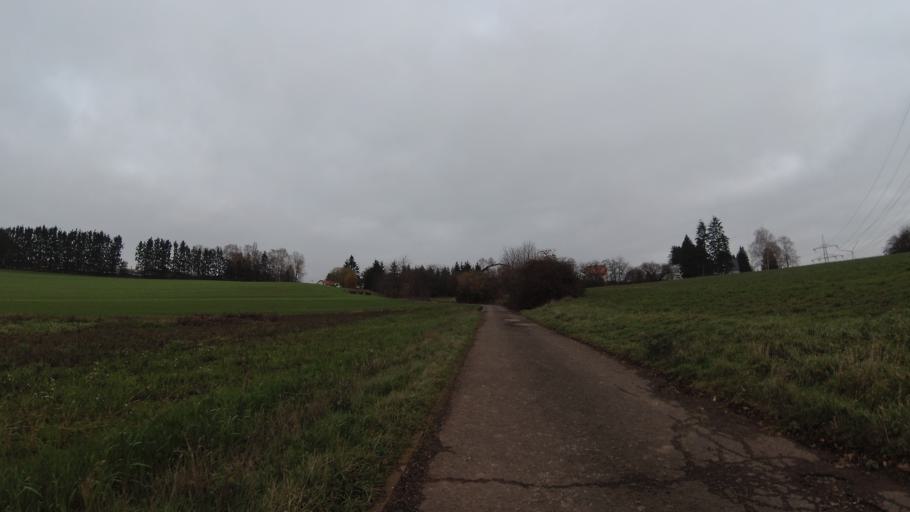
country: DE
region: Saarland
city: Schiffweiler
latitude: 49.3800
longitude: 7.1184
